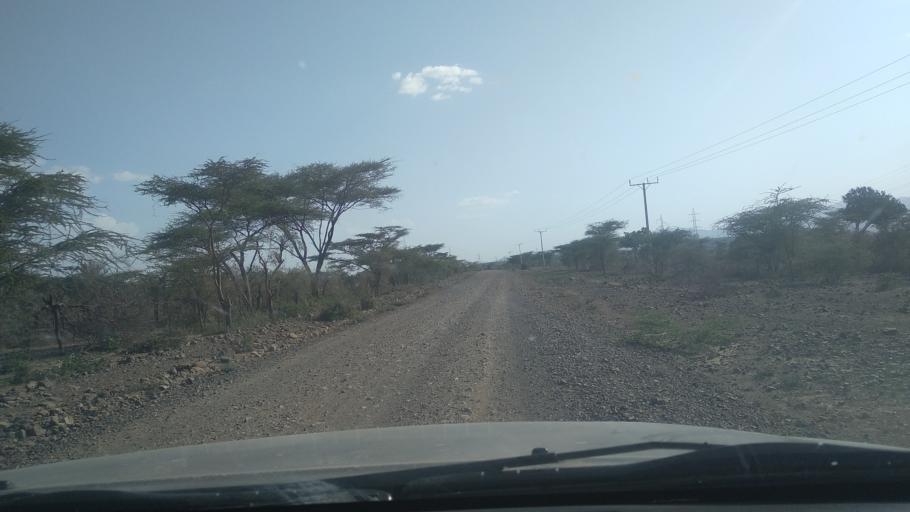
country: ET
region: Oromiya
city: Hirna
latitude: 9.4946
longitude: 41.0290
